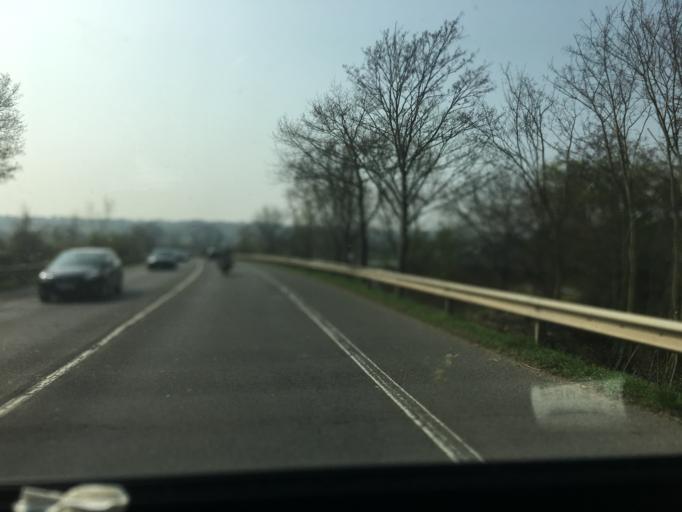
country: DE
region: North Rhine-Westphalia
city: Bornheim
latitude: 50.7684
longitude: 6.9754
